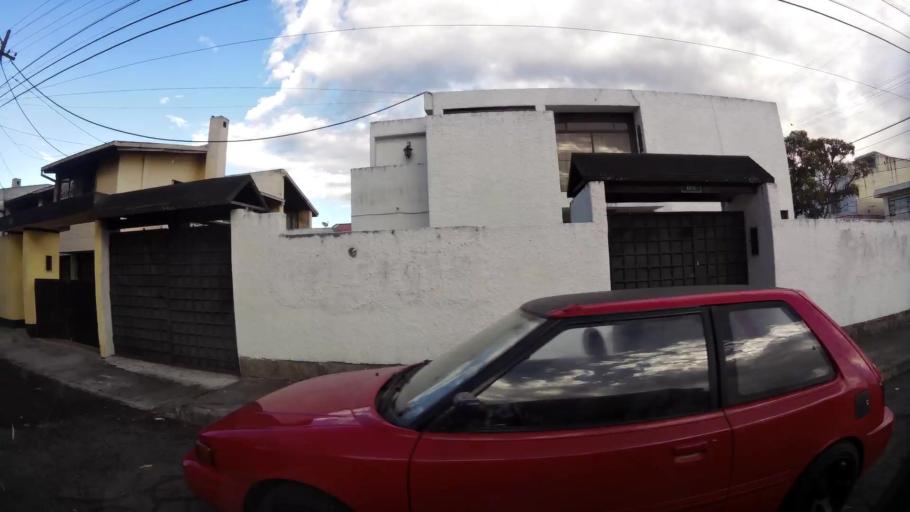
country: EC
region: Pichincha
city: Quito
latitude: -0.1559
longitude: -78.4818
